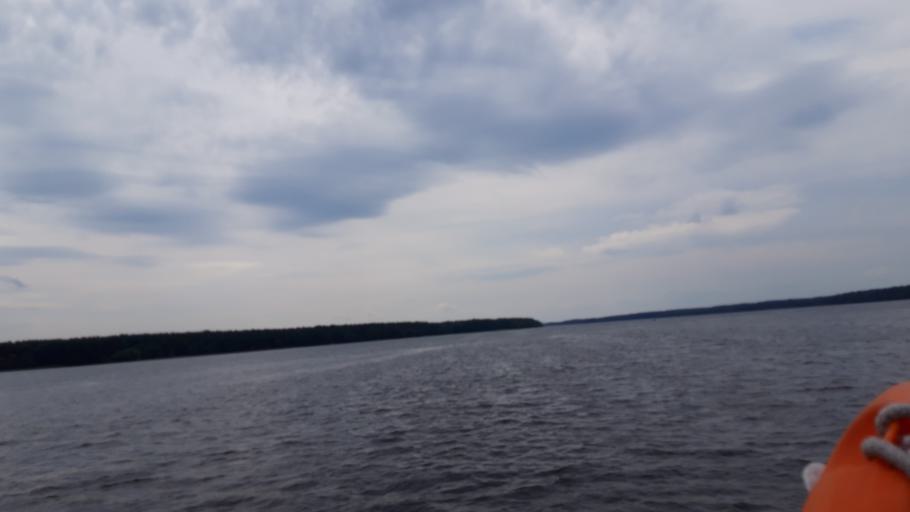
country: RU
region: Tverskaya
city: Konakovo
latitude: 56.7042
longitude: 36.7282
